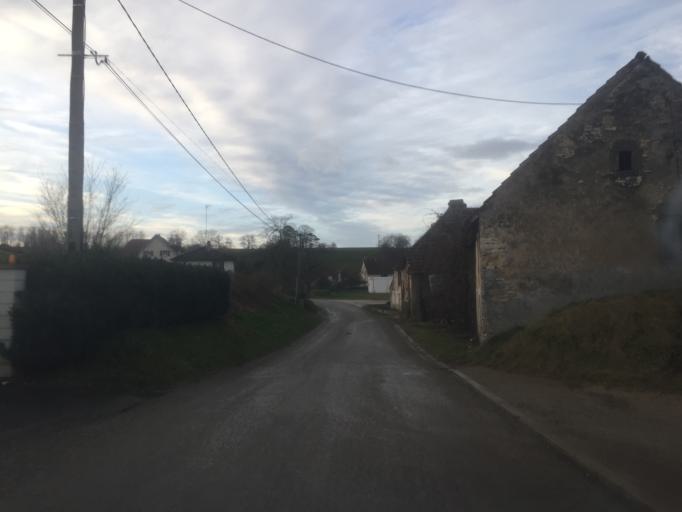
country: FR
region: Franche-Comte
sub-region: Departement du Jura
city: Orchamps
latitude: 47.1287
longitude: 5.6632
